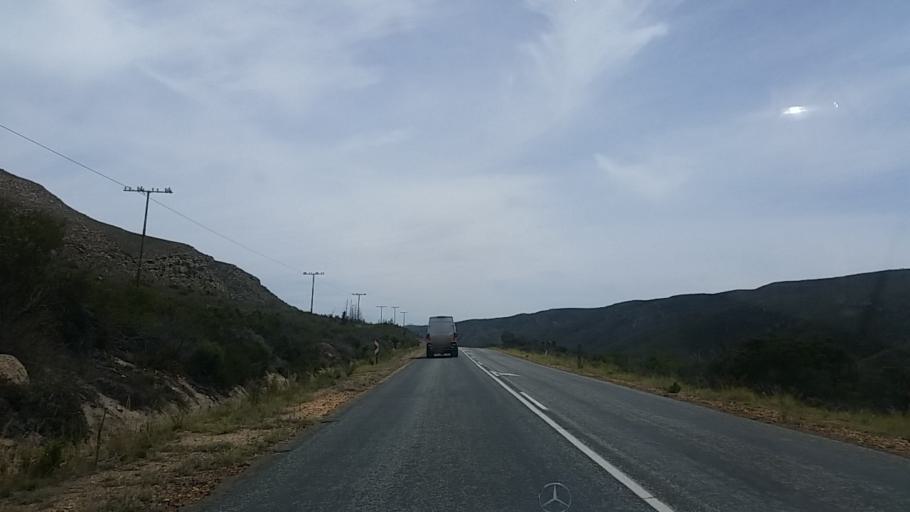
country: ZA
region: Western Cape
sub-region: Eden District Municipality
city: Knysna
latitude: -33.7428
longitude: 23.0181
